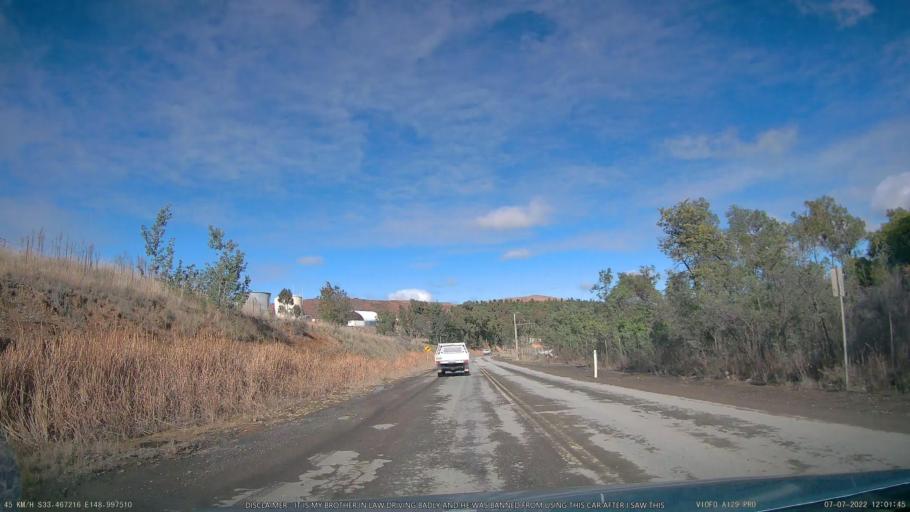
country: AU
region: New South Wales
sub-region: Blayney
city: Millthorpe
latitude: -33.4675
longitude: 148.9974
